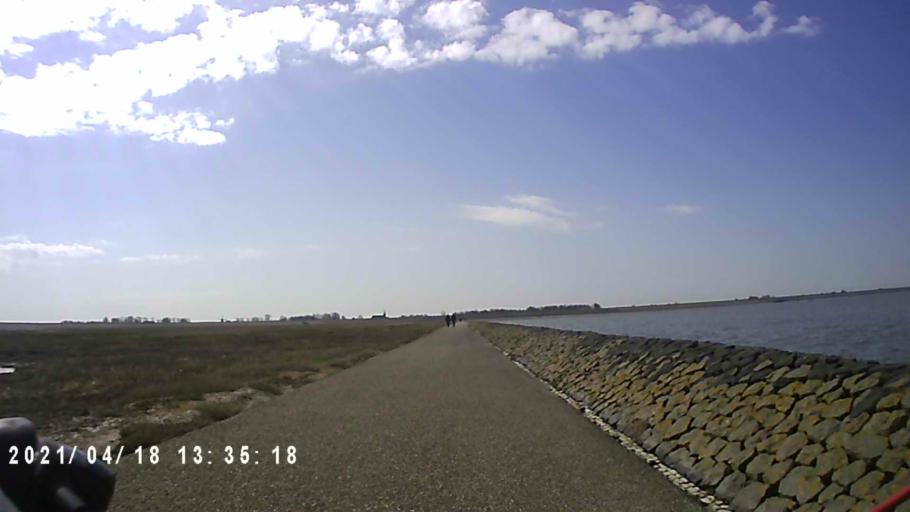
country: NL
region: Friesland
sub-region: Gemeente Dongeradeel
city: Anjum
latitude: 53.4087
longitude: 6.0911
